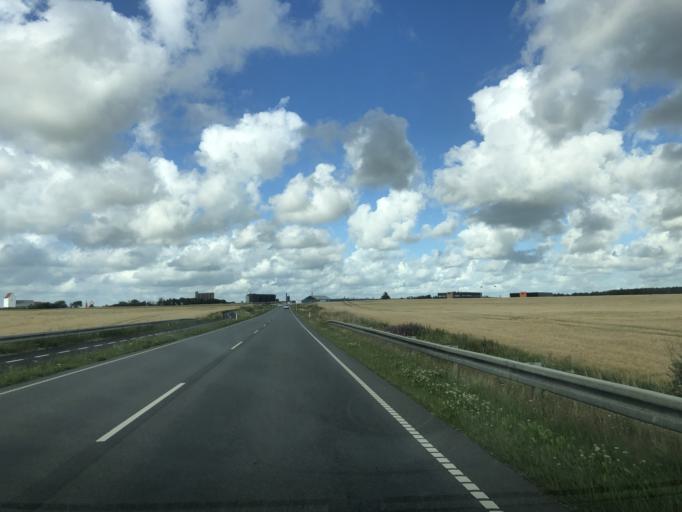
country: DK
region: Central Jutland
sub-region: Lemvig Kommune
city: Lemvig
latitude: 56.5113
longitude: 8.2982
